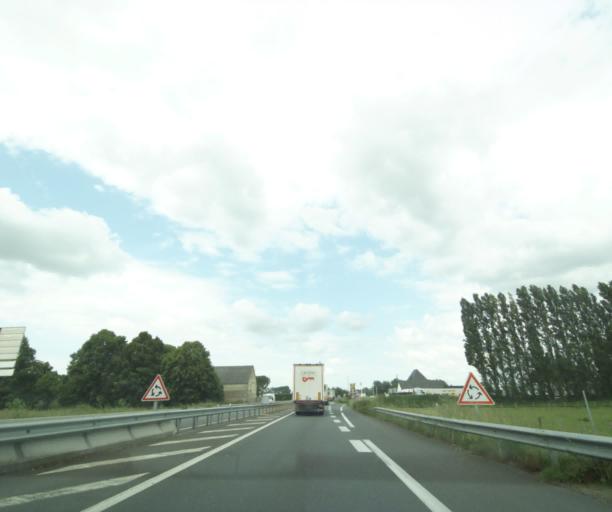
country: FR
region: Pays de la Loire
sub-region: Departement de Maine-et-Loire
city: Vivy
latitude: 47.3031
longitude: -0.0368
